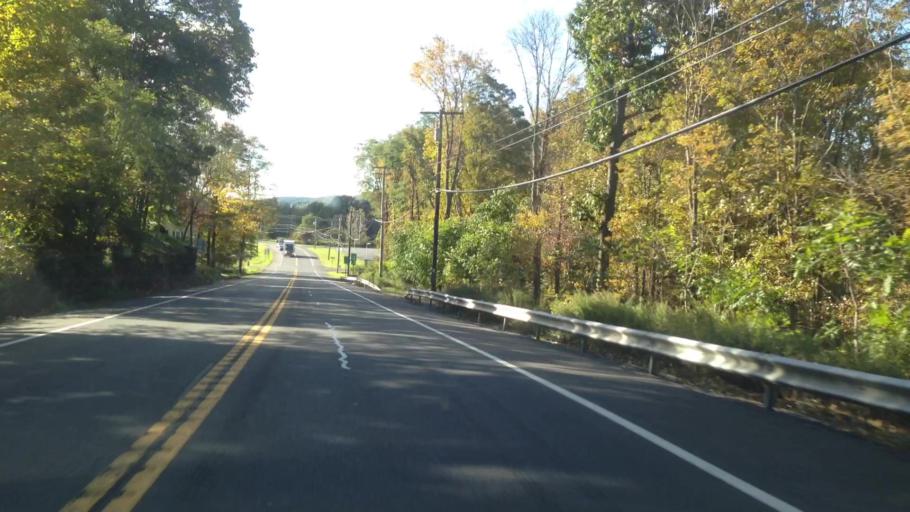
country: US
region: New York
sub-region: Dutchess County
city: Hyde Park
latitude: 41.8291
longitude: -73.9668
